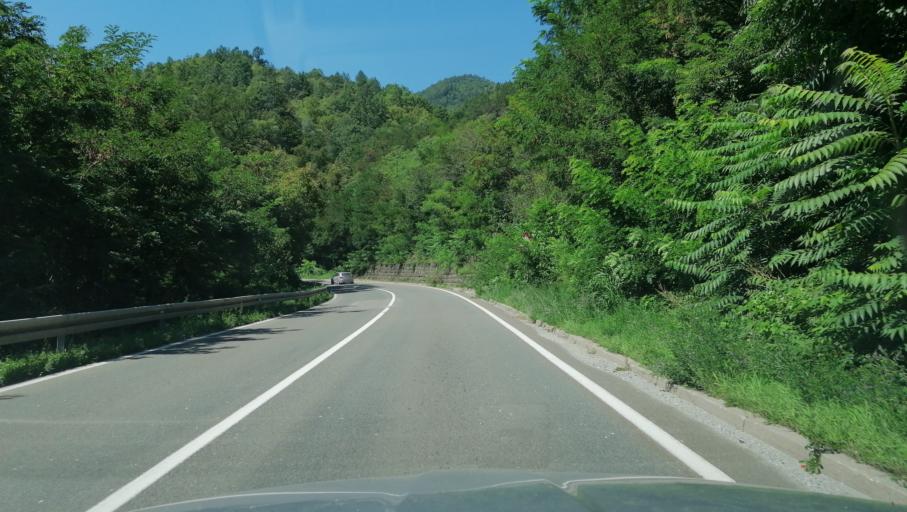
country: RS
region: Central Serbia
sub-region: Raski Okrug
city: Kraljevo
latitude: 43.6157
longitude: 20.5498
